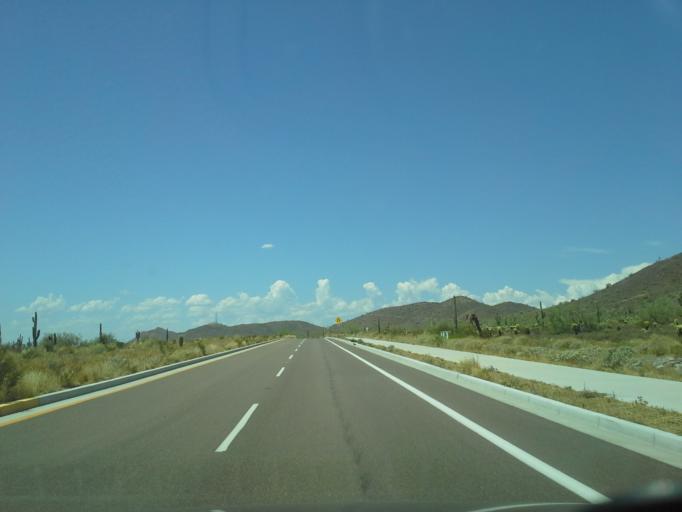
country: US
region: Arizona
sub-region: Maricopa County
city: Cave Creek
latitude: 33.7691
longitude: -112.0600
